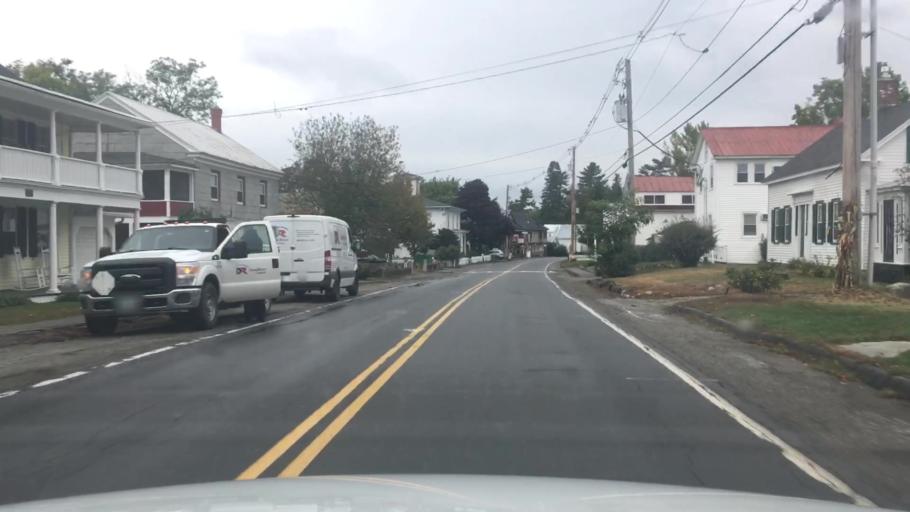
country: US
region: Maine
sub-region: Kennebec County
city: Rome
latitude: 44.5278
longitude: -69.8877
